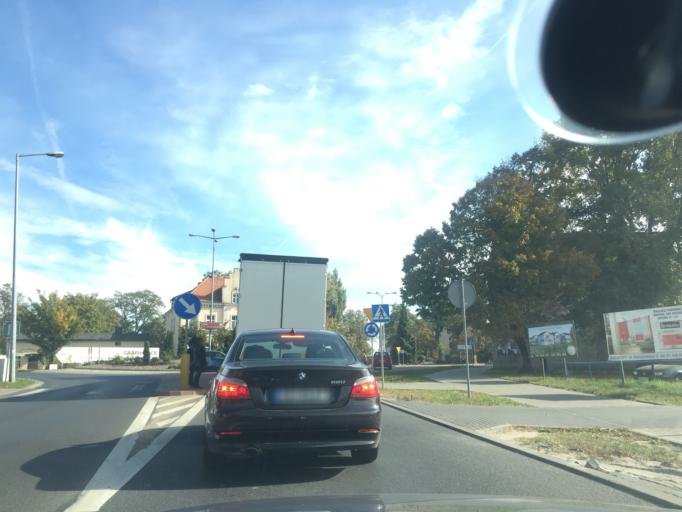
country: PL
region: Greater Poland Voivodeship
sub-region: Powiat wrzesinski
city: Wrzesnia
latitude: 52.3292
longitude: 17.5626
